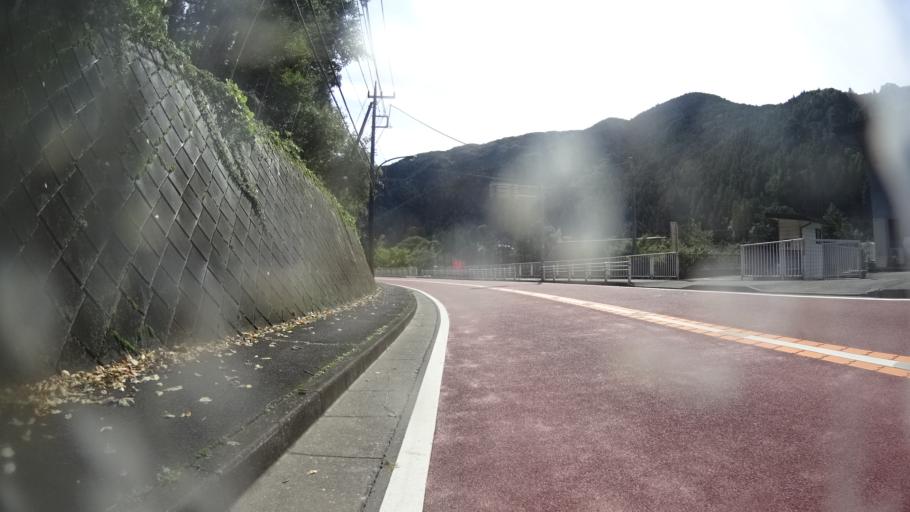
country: JP
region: Tokyo
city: Ome
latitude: 35.8128
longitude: 139.1556
